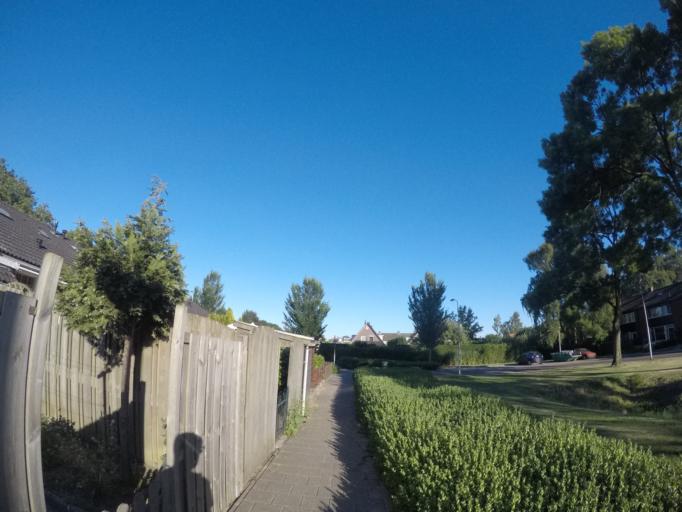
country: NL
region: Gelderland
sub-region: Gemeente Westervoort
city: Westervoort
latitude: 51.9583
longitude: 5.9656
